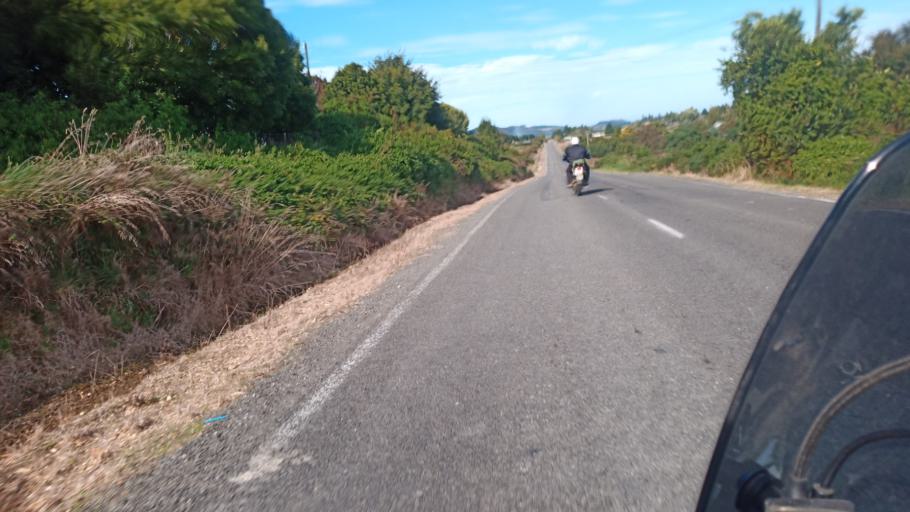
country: NZ
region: Hawke's Bay
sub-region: Wairoa District
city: Wairoa
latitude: -39.0664
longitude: 177.1364
